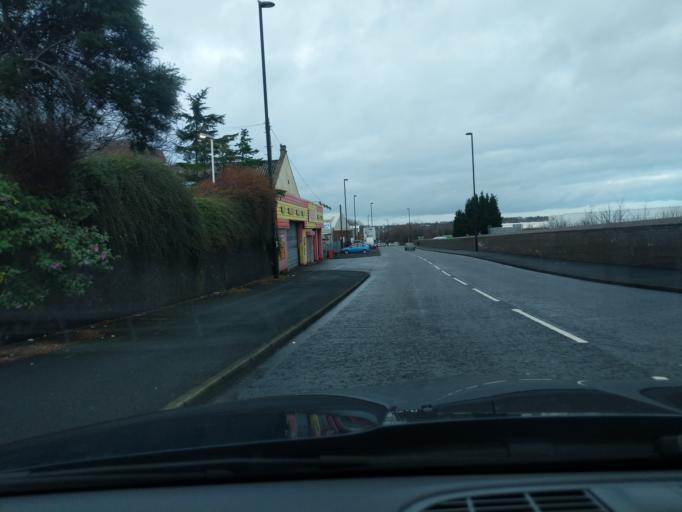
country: GB
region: England
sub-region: Gateshead
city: Felling
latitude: 54.9785
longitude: -1.5739
